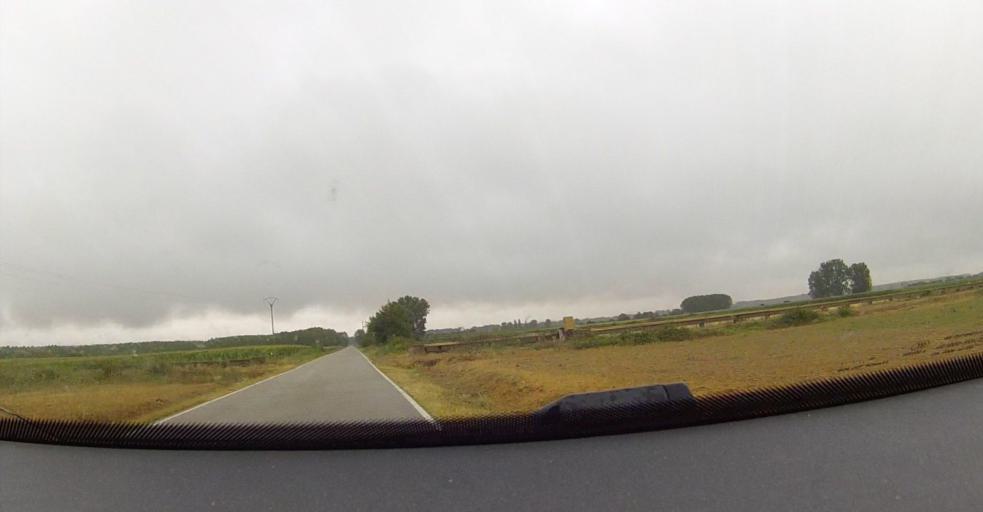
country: ES
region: Castille and Leon
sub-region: Provincia de Palencia
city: Pedrosa de la Vega
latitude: 42.4803
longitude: -4.7329
